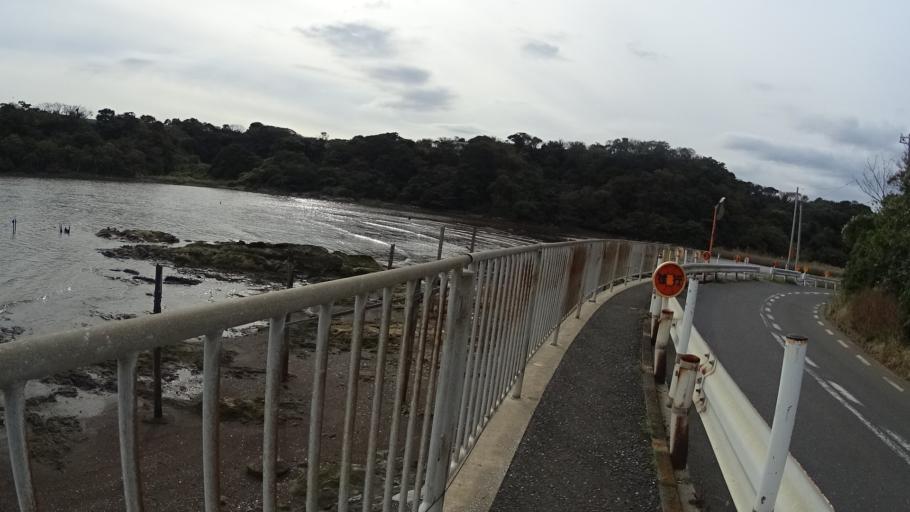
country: JP
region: Kanagawa
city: Miura
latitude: 35.1445
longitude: 139.6638
